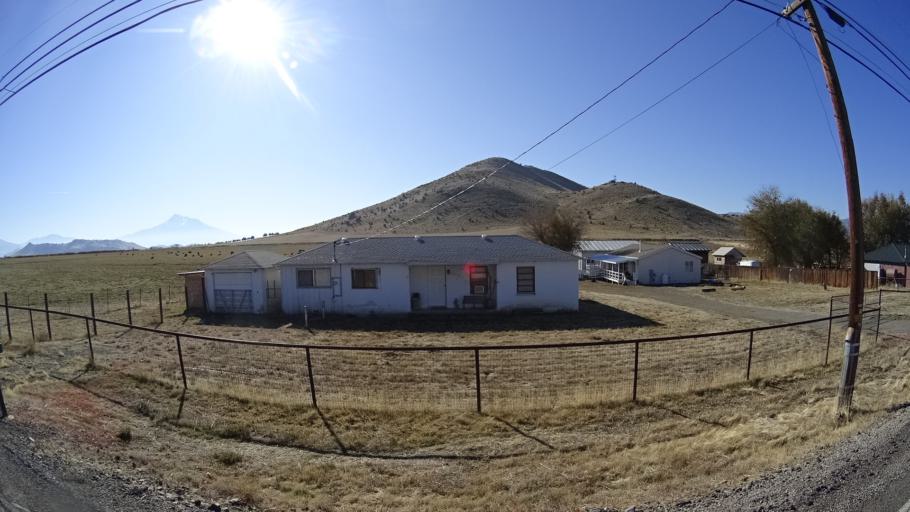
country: US
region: California
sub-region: Siskiyou County
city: Montague
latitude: 41.7249
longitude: -122.5130
